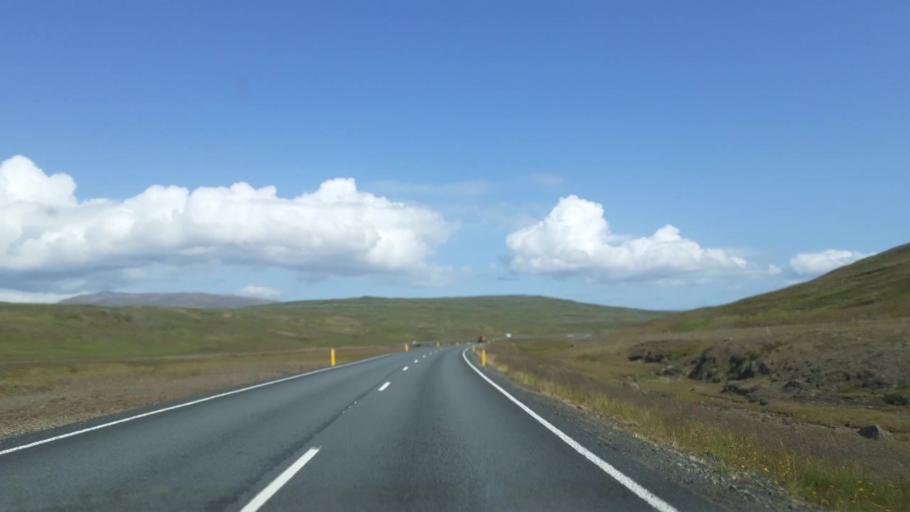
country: IS
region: West
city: Borgarnes
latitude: 64.8989
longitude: -21.1868
